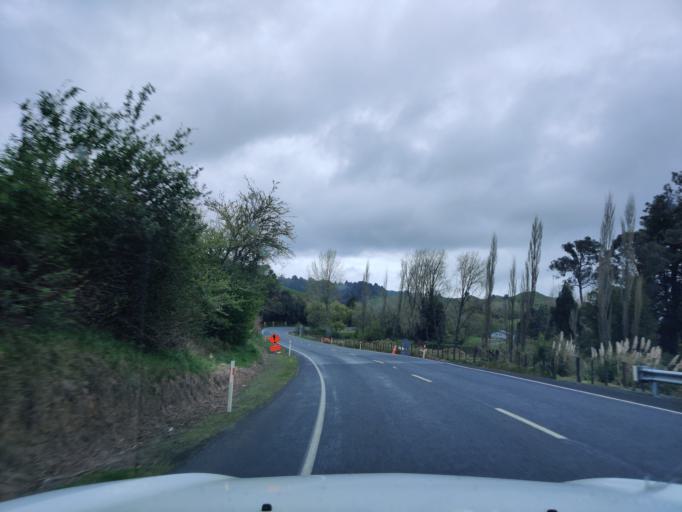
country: NZ
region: Waikato
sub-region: Otorohanga District
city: Otorohanga
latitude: -38.6073
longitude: 175.2170
